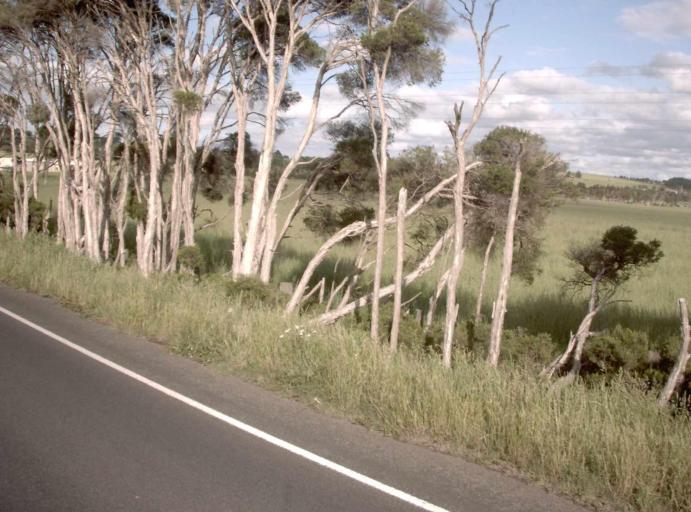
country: AU
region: Victoria
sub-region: Baw Baw
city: Warragul
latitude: -38.4929
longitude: 145.9280
